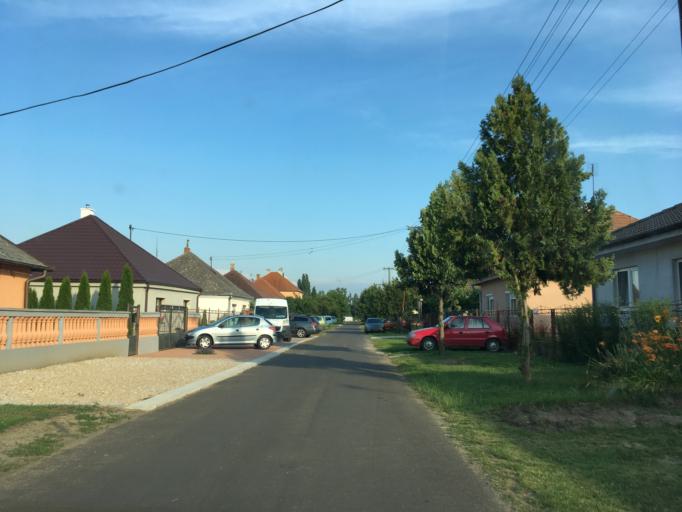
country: SK
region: Nitriansky
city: Svodin
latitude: 47.8989
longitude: 18.4099
